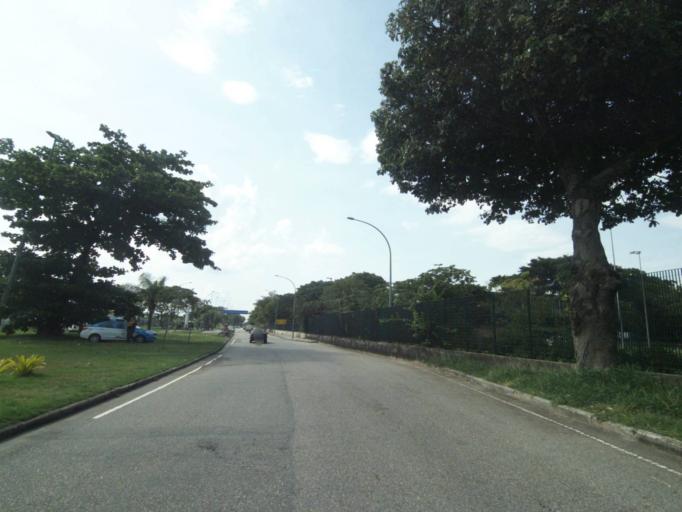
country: BR
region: Rio de Janeiro
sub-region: Rio De Janeiro
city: Rio de Janeiro
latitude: -22.8595
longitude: -43.2328
